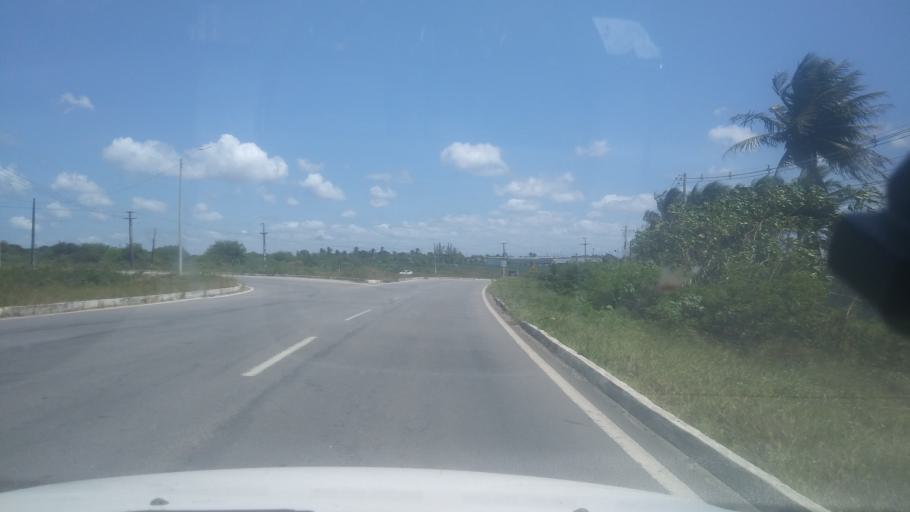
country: BR
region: Rio Grande do Norte
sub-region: Extremoz
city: Extremoz
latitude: -5.7216
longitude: -35.2782
